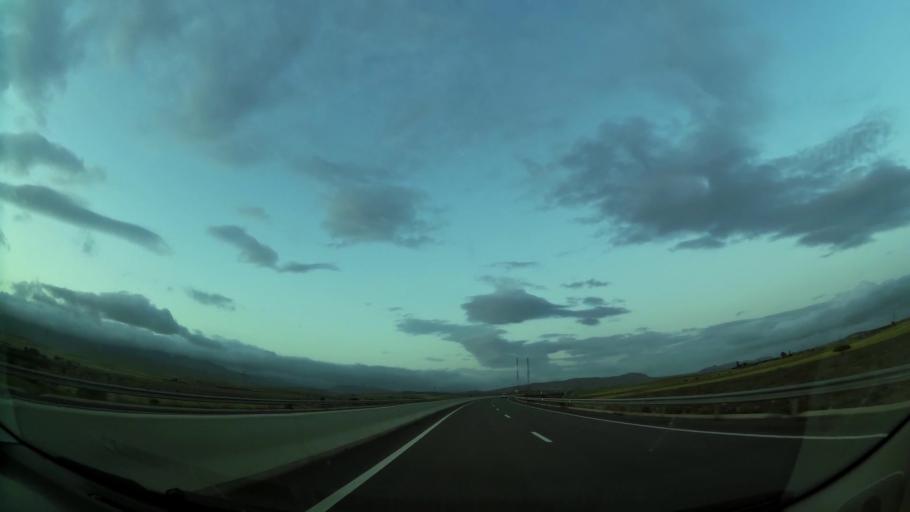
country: MA
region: Oriental
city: El Aioun
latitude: 34.6217
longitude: -2.5464
